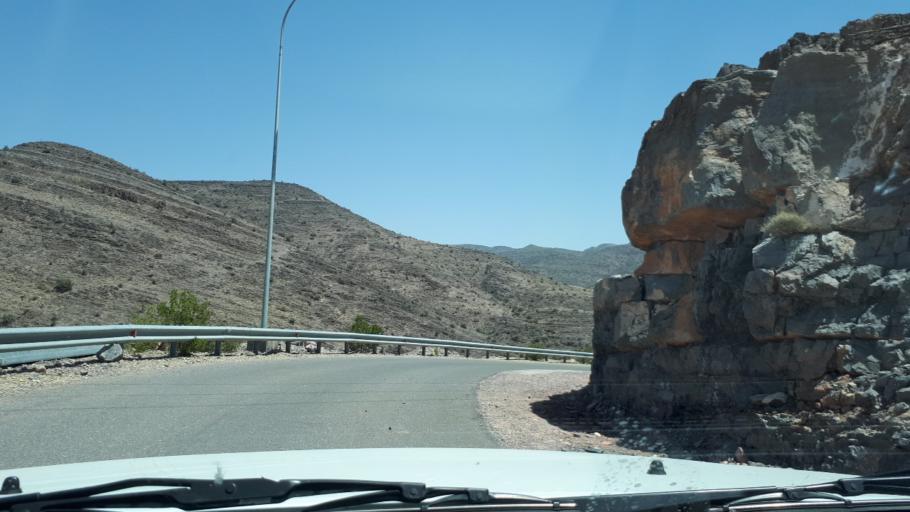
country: OM
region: Muhafazat ad Dakhiliyah
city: Izki
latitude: 23.0824
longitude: 57.7173
